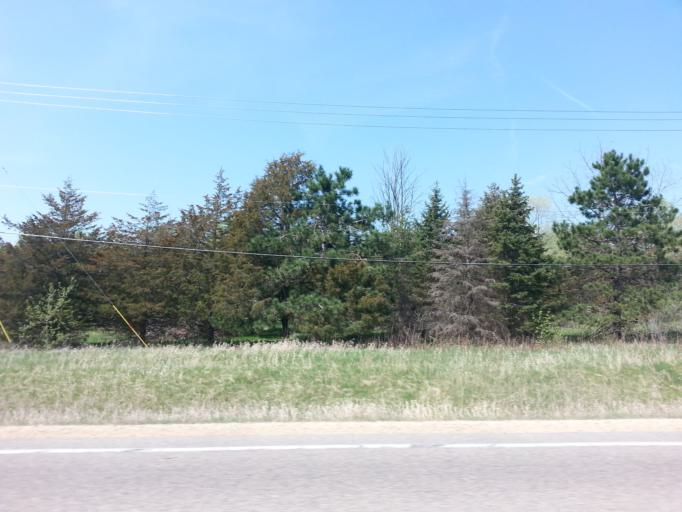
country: US
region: Minnesota
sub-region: Washington County
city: Lake Saint Croix Beach
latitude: 44.9371
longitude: -92.7711
